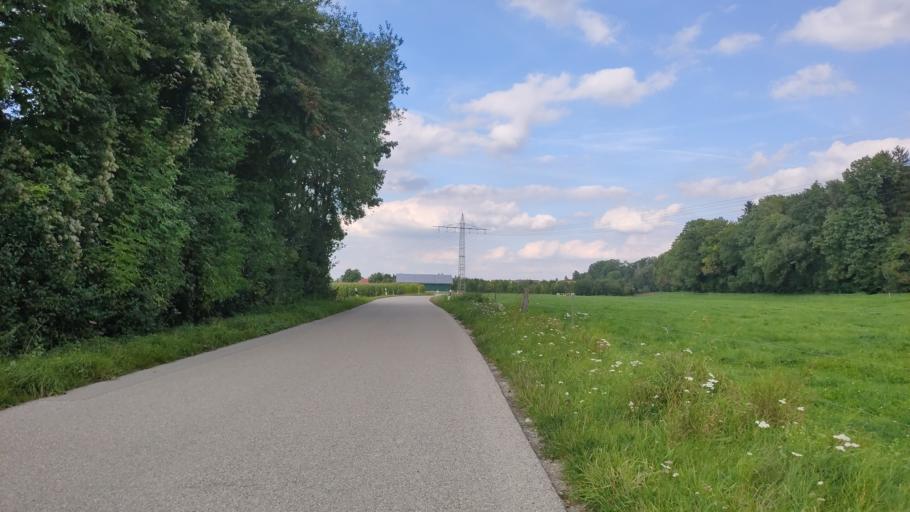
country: DE
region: Bavaria
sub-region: Upper Bavaria
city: Scheuring
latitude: 48.1612
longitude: 10.8835
